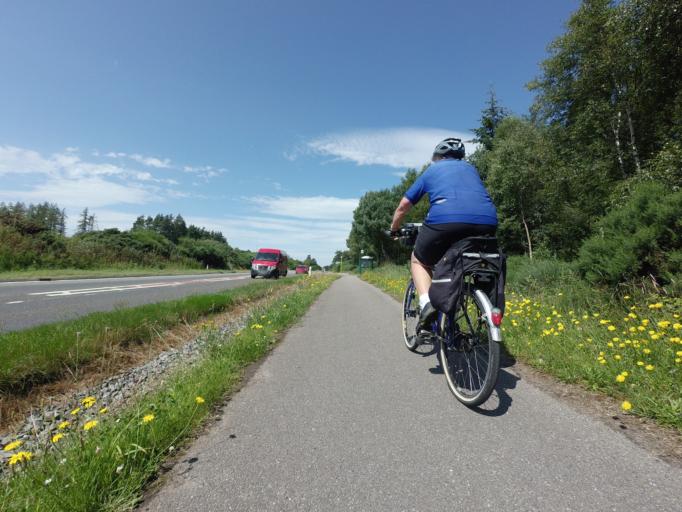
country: GB
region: Scotland
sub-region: Highland
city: Conon Bridge
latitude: 57.5411
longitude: -4.3747
